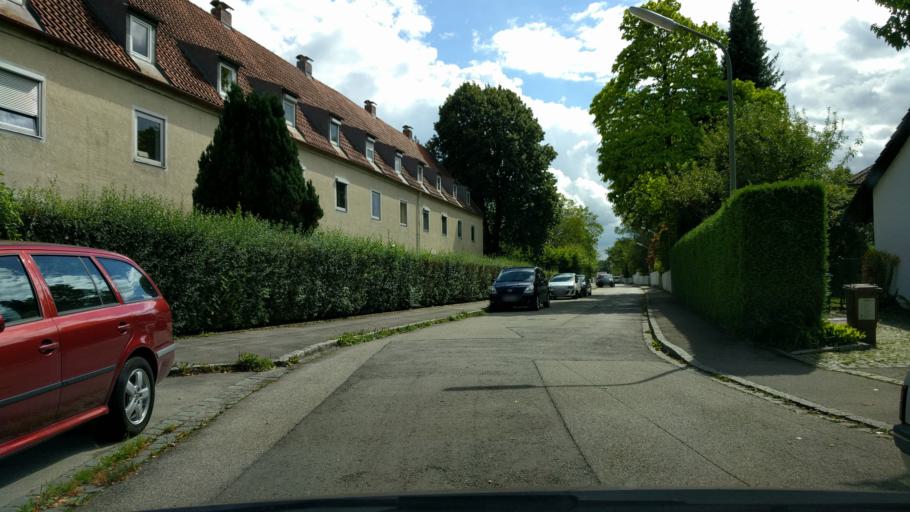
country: DE
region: Bavaria
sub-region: Upper Bavaria
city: Grunwald
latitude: 48.0393
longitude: 11.5331
